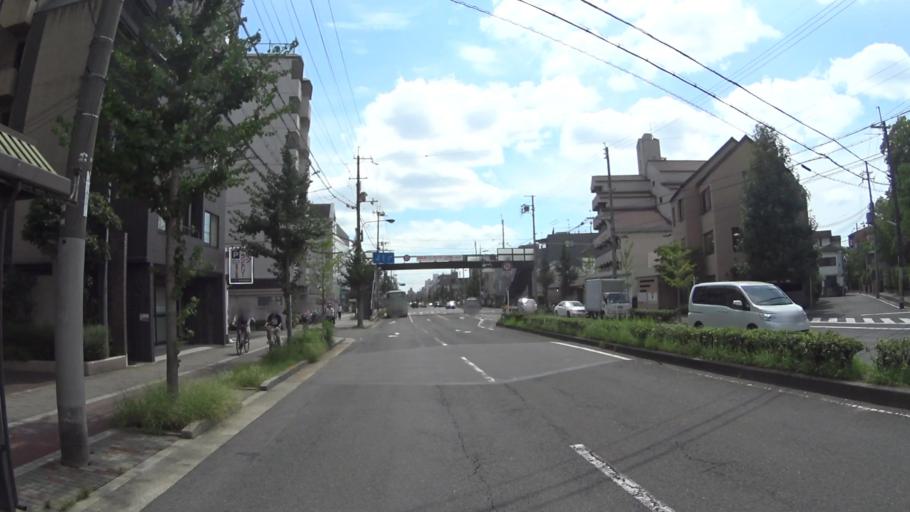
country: JP
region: Kyoto
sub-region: Kyoto-shi
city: Kamigyo-ku
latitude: 35.0381
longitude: 135.7820
